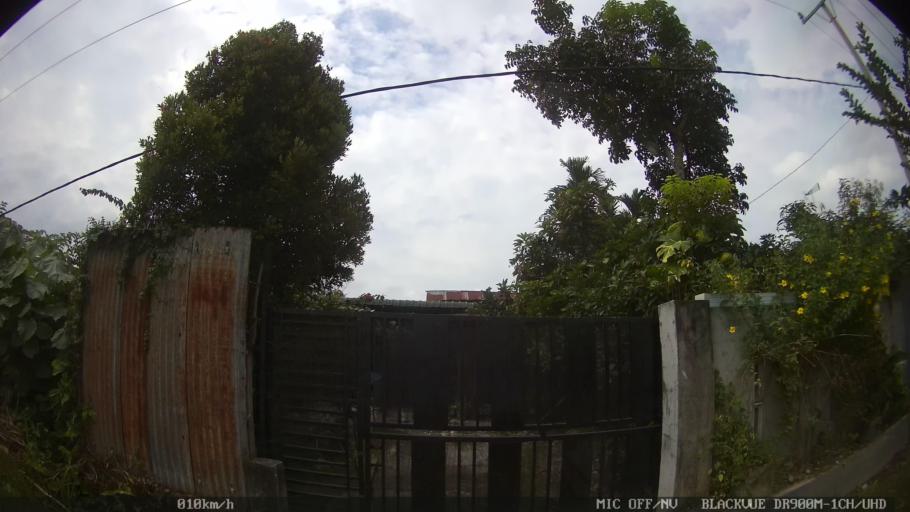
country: ID
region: North Sumatra
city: Sunggal
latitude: 3.6240
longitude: 98.5986
